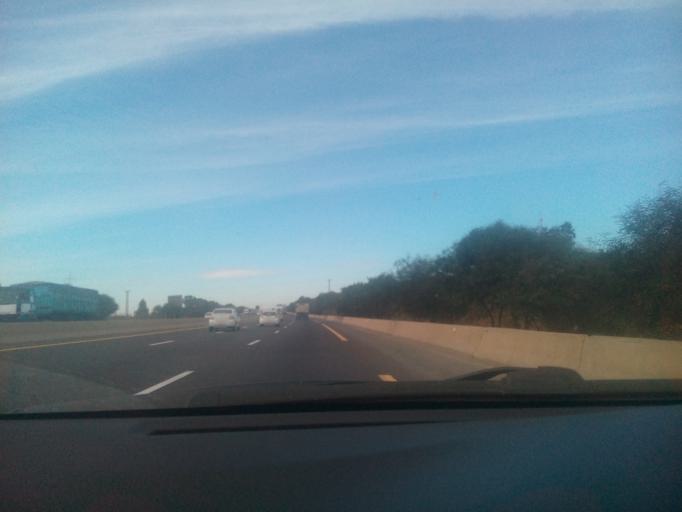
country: DZ
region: Oran
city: Sidi ech Chahmi
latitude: 35.5726
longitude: -0.5423
